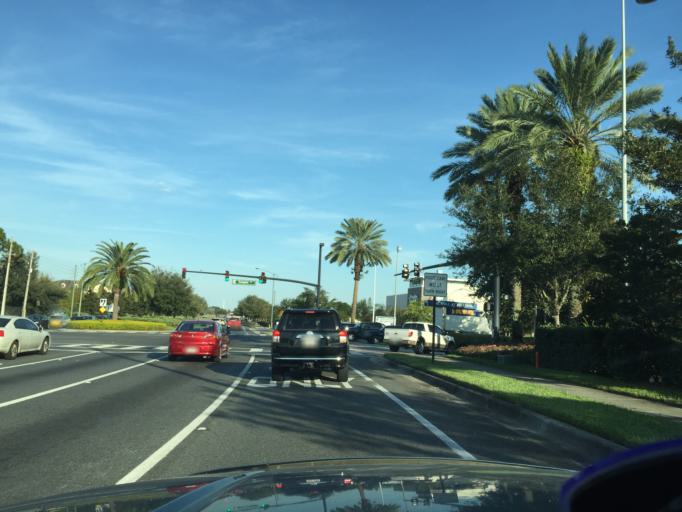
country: US
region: Florida
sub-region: Orange County
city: Oak Ridge
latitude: 28.4867
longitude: -81.4272
